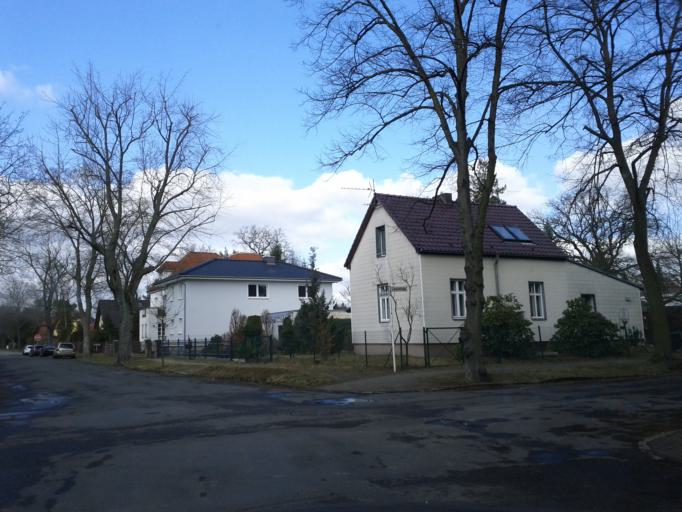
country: DE
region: Brandenburg
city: Schoneiche
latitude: 52.4684
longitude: 13.6862
